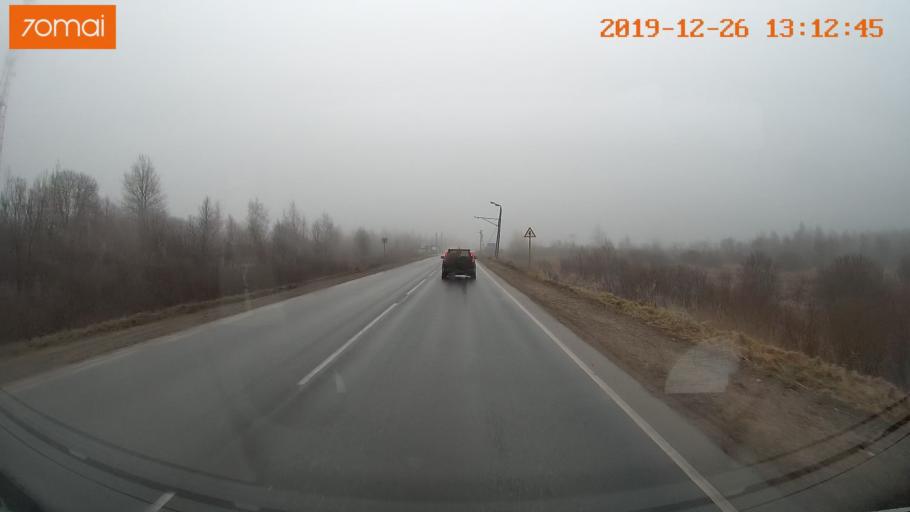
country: RU
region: Vologda
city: Cherepovets
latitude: 59.0217
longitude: 38.0403
